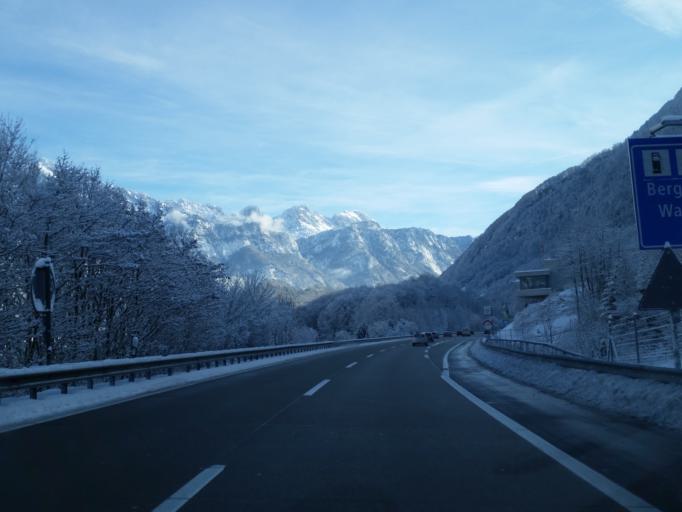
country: CH
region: Saint Gallen
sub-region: Wahlkreis Sarganserland
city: Quarten
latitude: 47.1133
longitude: 9.2641
